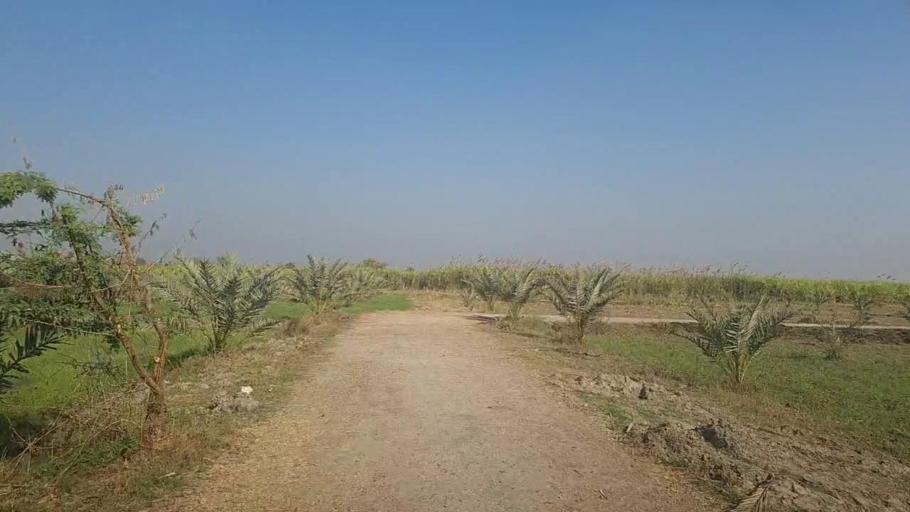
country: PK
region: Sindh
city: Kot Diji
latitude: 27.4338
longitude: 68.7329
